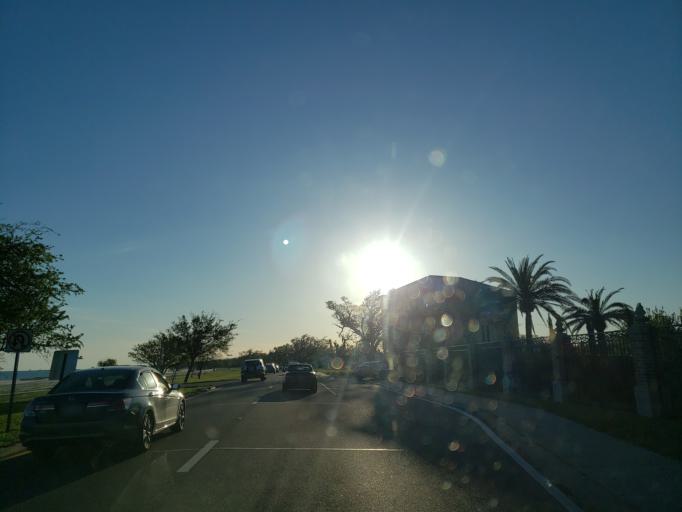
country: US
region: Mississippi
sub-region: Harrison County
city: Gulfport
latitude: 30.3570
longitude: -89.1172
